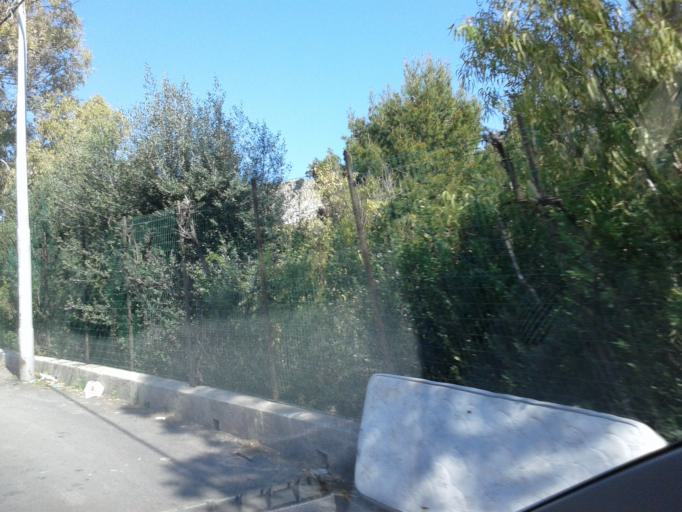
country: IT
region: Sicily
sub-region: Palermo
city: Piano dei Geli
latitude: 38.1151
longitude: 13.2941
